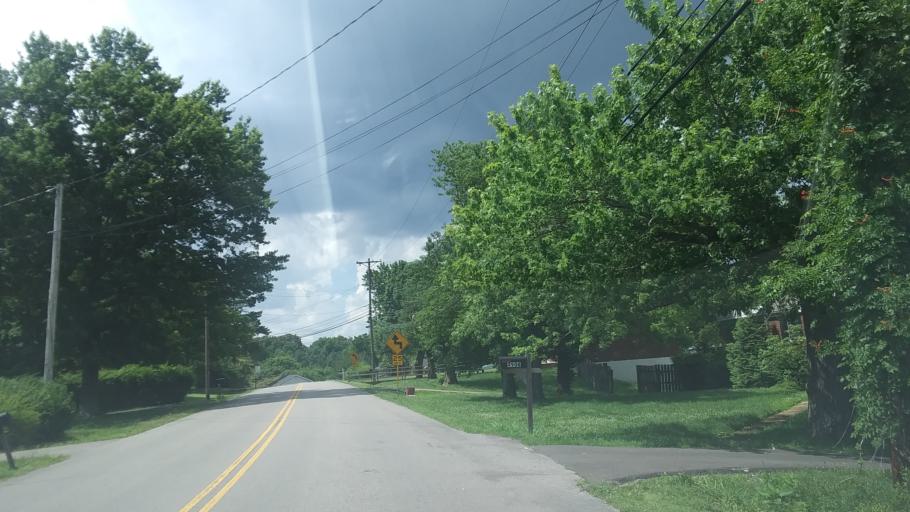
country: US
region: Tennessee
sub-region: Davidson County
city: Oak Hill
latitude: 36.0741
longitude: -86.7161
